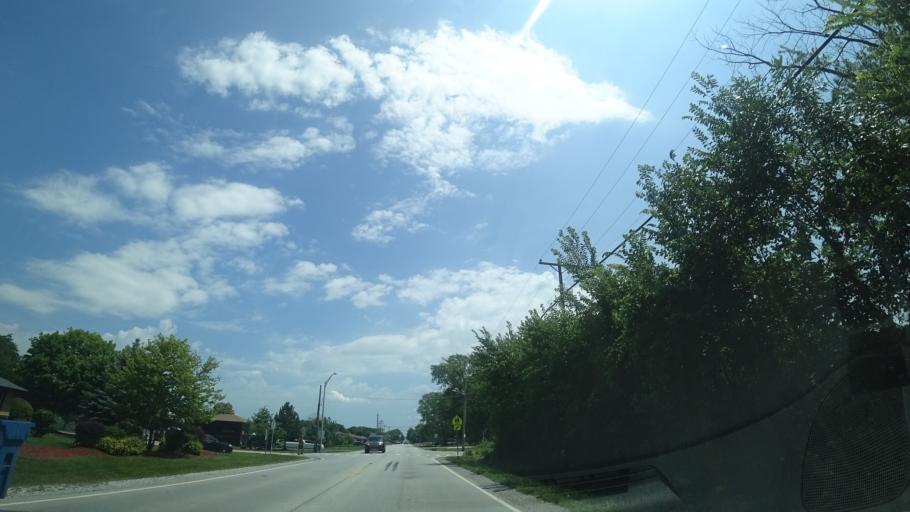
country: US
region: Illinois
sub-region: Cook County
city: Crestwood
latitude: 41.6612
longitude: -87.7685
